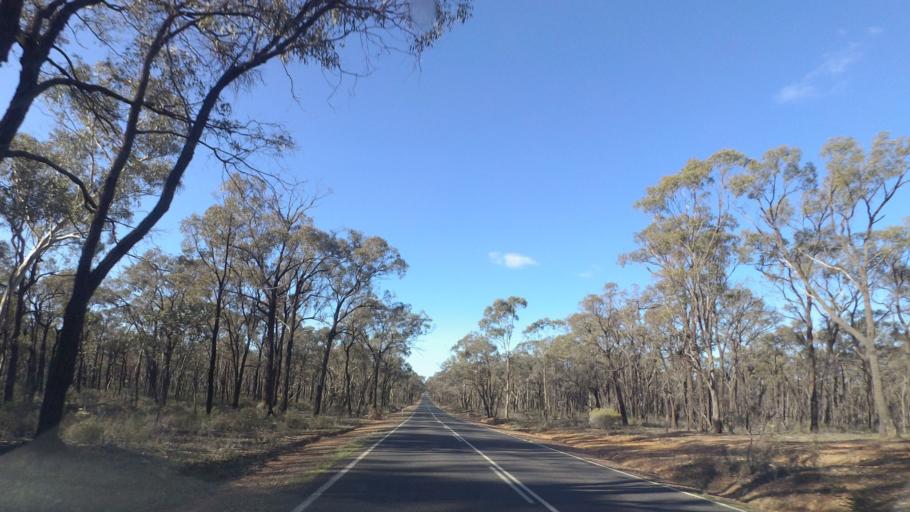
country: AU
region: Victoria
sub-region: Greater Bendigo
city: Epsom
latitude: -36.6646
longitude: 144.4432
